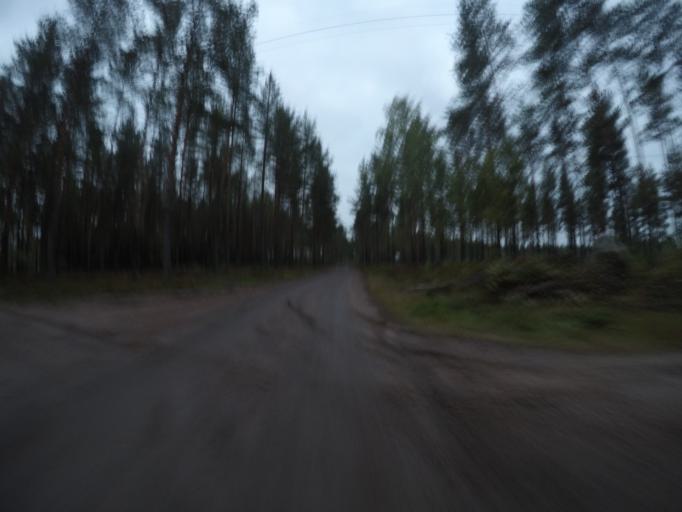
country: SE
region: Vaestmanland
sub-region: Kungsors Kommun
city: Kungsoer
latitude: 59.3787
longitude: 16.1174
